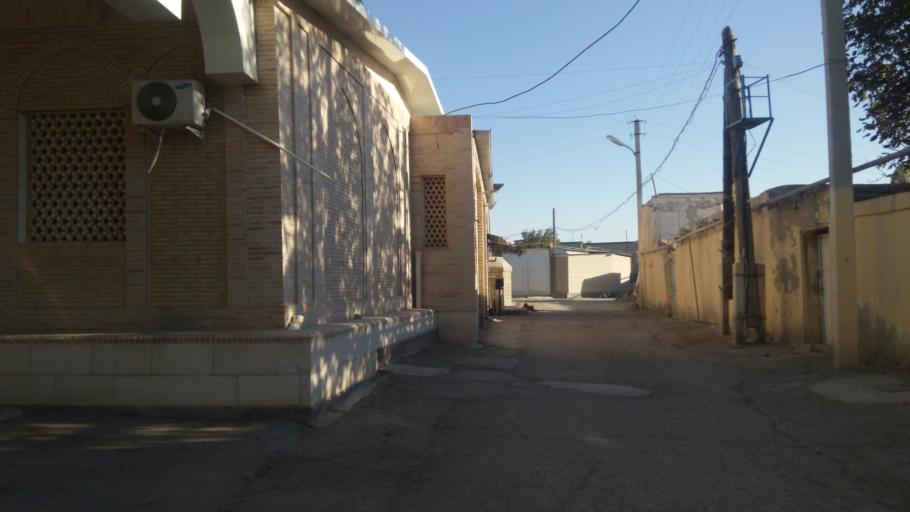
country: UZ
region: Bukhara
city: Bukhara
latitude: 39.7757
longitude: 64.4255
